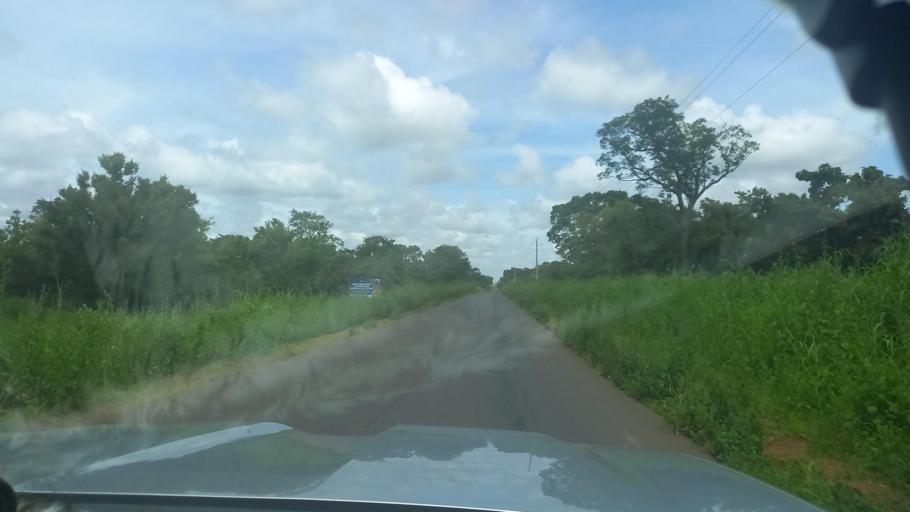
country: GM
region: Lower River
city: Kaiaf
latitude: 13.2112
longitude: -15.5460
